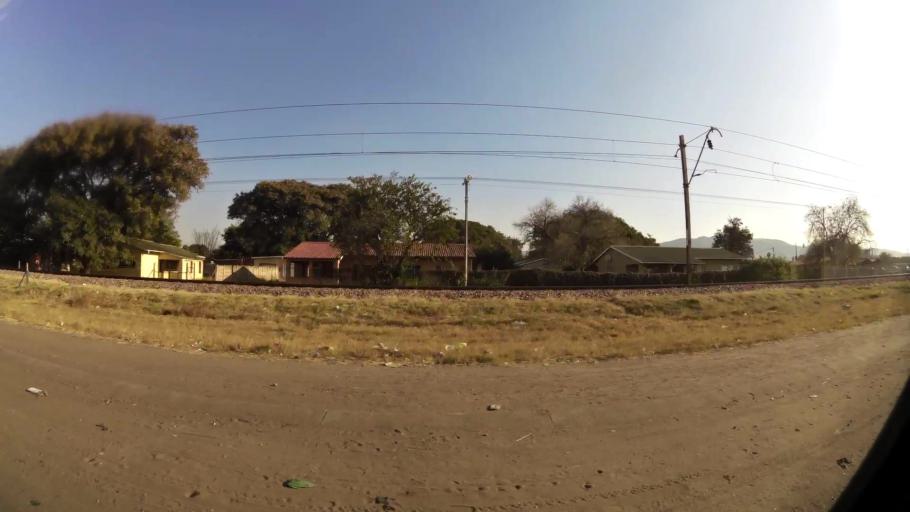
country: ZA
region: North-West
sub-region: Bojanala Platinum District Municipality
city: Rustenburg
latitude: -25.6443
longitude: 27.2312
